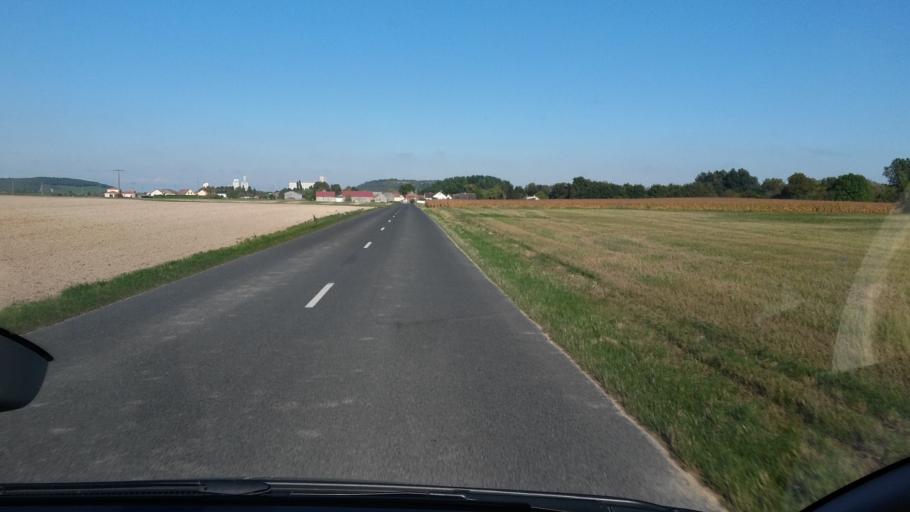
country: FR
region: Champagne-Ardenne
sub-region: Departement de la Marne
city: Vertus
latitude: 48.8373
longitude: 3.9531
